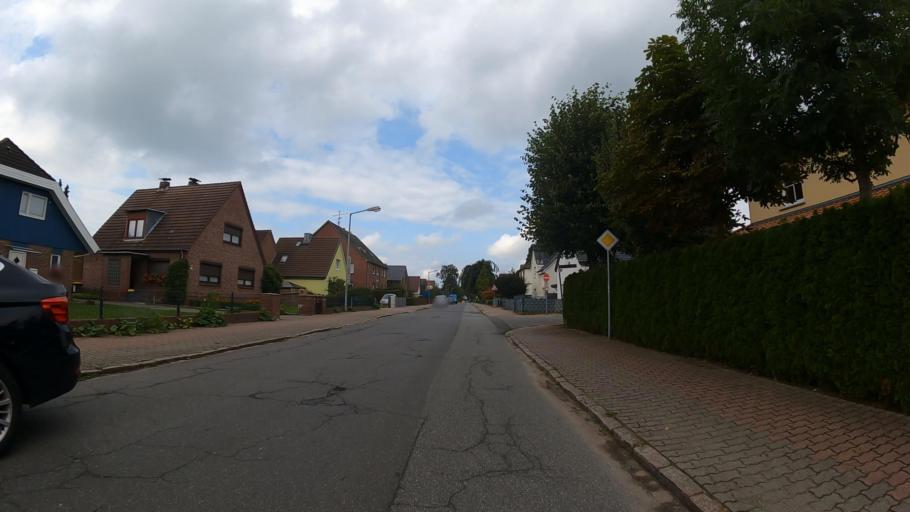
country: DE
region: Schleswig-Holstein
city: Tornesch
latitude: 53.7015
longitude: 9.7159
